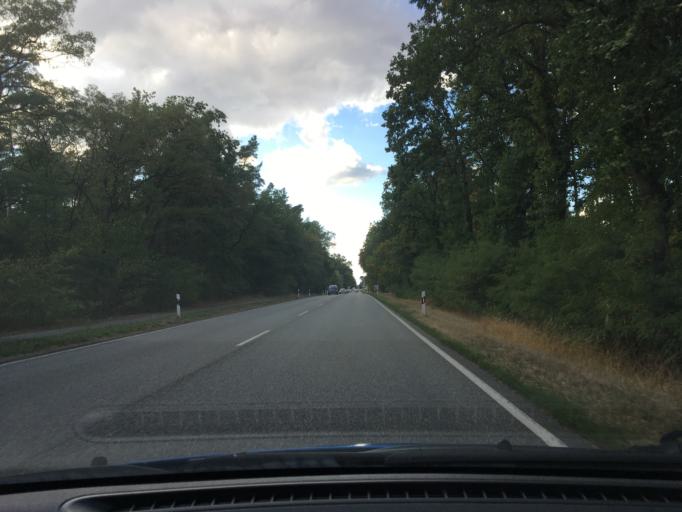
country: DE
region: Mecklenburg-Vorpommern
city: Ludwigslust
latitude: 53.3129
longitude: 11.5110
